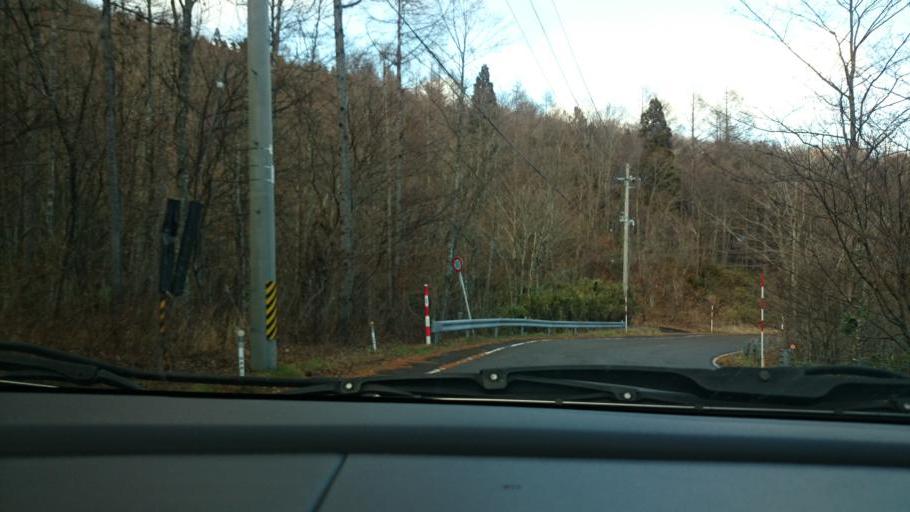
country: JP
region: Tochigi
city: Kuroiso
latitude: 37.1569
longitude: 140.0166
